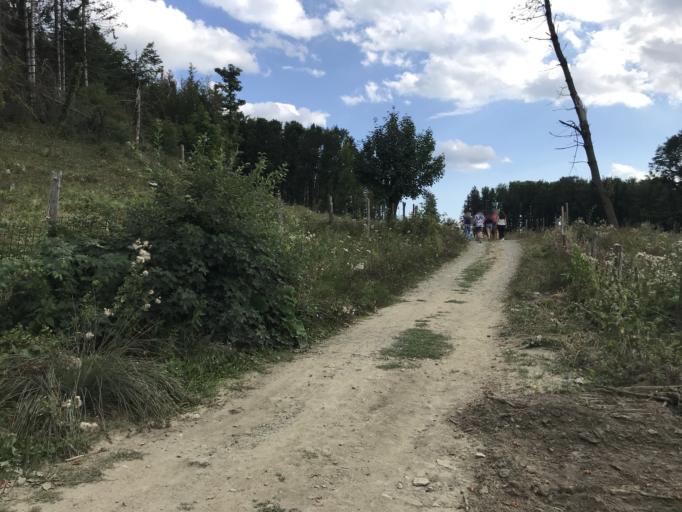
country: IT
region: Emilia-Romagna
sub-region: Provincia di Bologna
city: San Benedetto Val di Sambro
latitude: 44.1512
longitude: 11.2620
